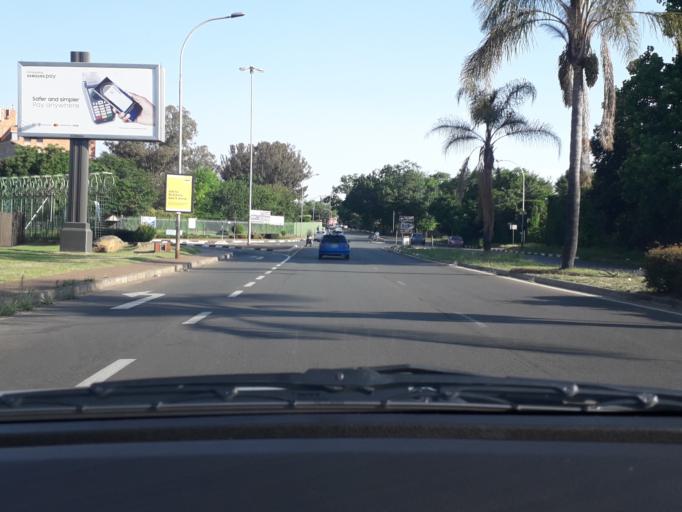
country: ZA
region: Gauteng
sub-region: City of Johannesburg Metropolitan Municipality
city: Johannesburg
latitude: -26.1813
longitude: 28.1040
